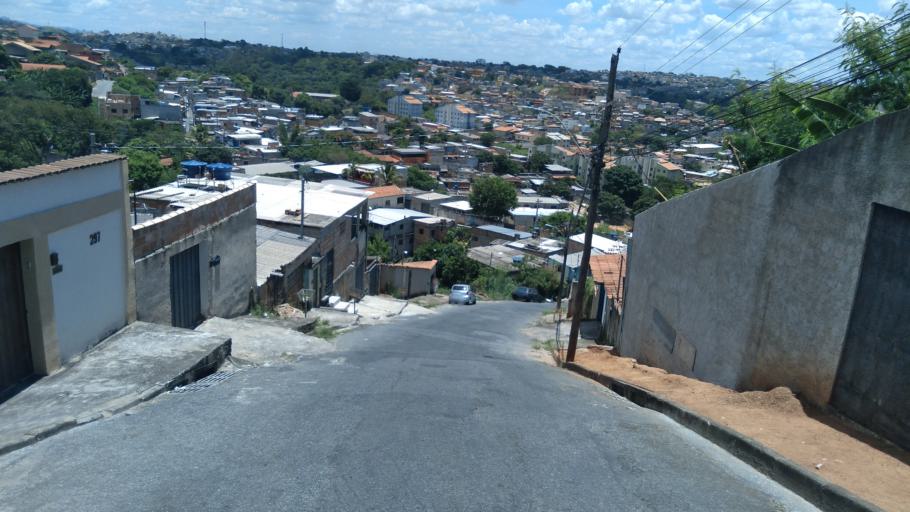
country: BR
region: Minas Gerais
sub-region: Santa Luzia
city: Santa Luzia
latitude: -19.8421
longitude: -43.8965
